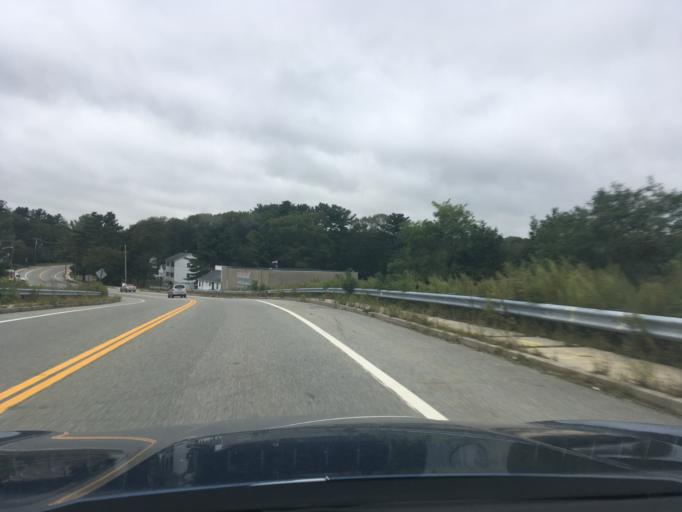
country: US
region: Rhode Island
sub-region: Kent County
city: East Greenwich
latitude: 41.6145
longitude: -71.4744
